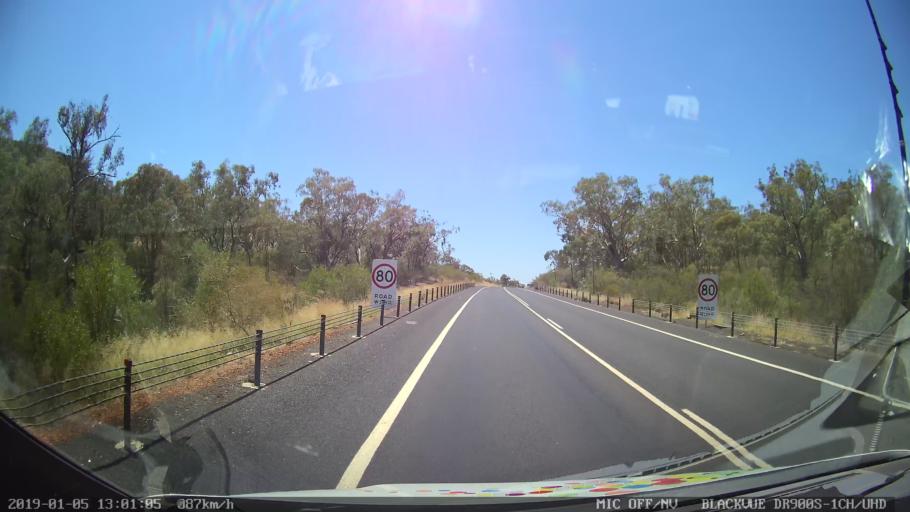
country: AU
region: New South Wales
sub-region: Narrabri
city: Boggabri
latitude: -31.1143
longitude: 149.7924
